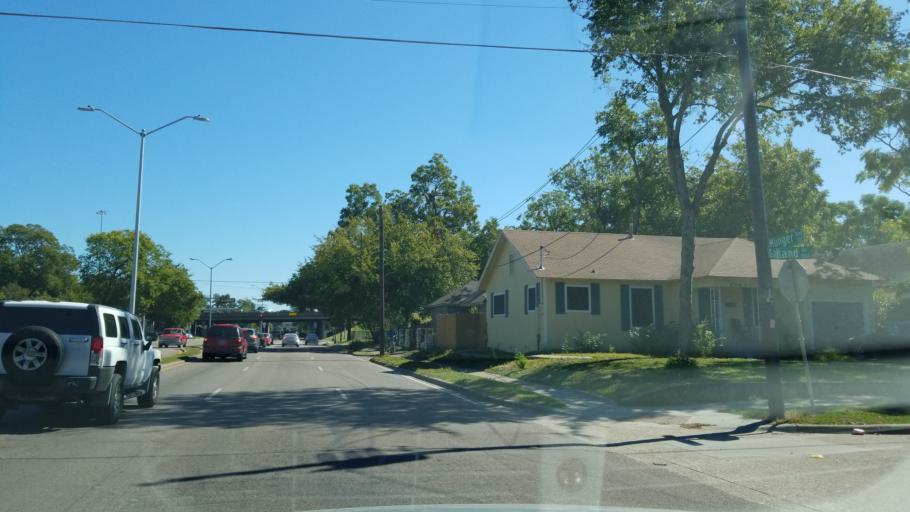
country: US
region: Texas
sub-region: Dallas County
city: Dallas
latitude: 32.7924
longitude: -96.7577
